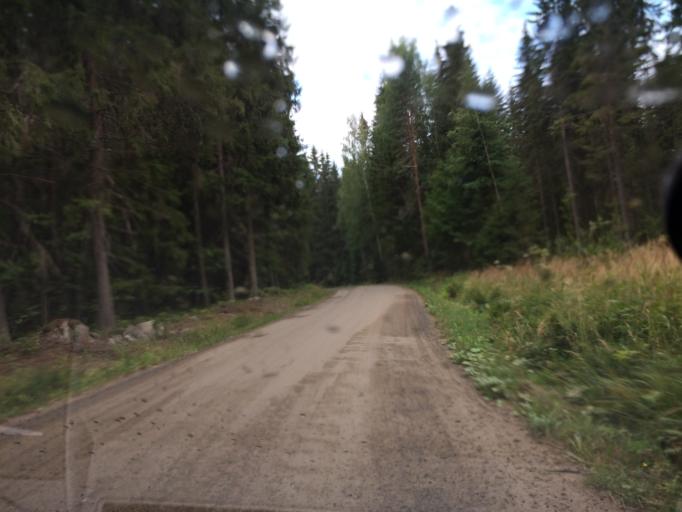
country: FI
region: Pirkanmaa
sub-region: Tampere
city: Luopioinen
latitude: 61.2729
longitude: 24.6724
